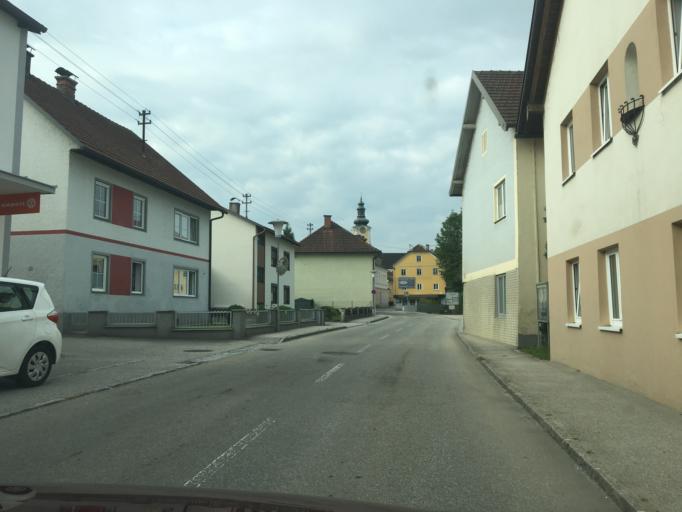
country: AT
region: Upper Austria
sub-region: Politischer Bezirk Grieskirchen
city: Grieskirchen
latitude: 48.3320
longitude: 13.8584
